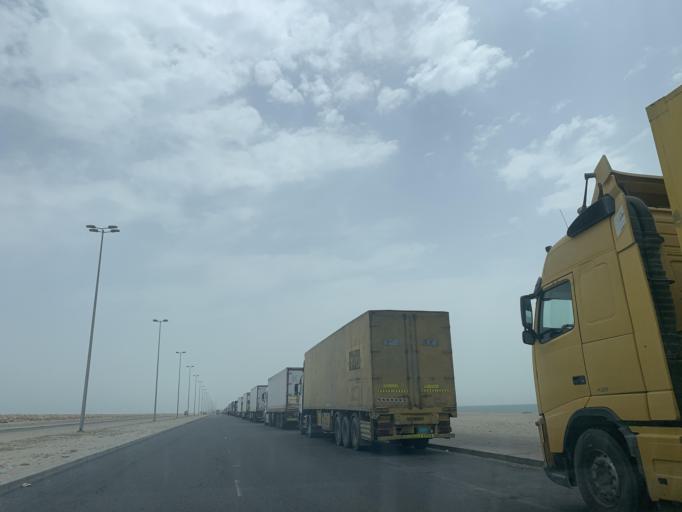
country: BH
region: Muharraq
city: Al Hadd
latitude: 26.2081
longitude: 50.7055
